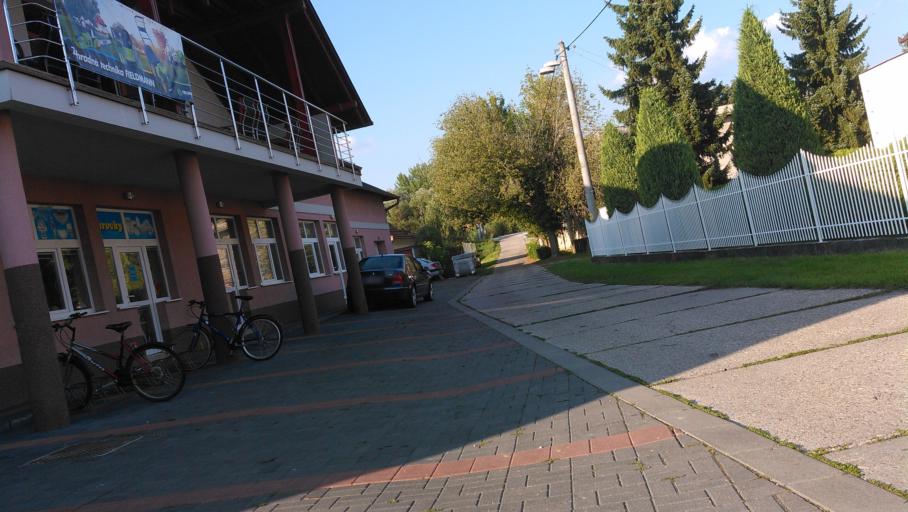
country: SK
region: Nitriansky
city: Kolarovo
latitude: 47.9204
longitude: 17.9964
